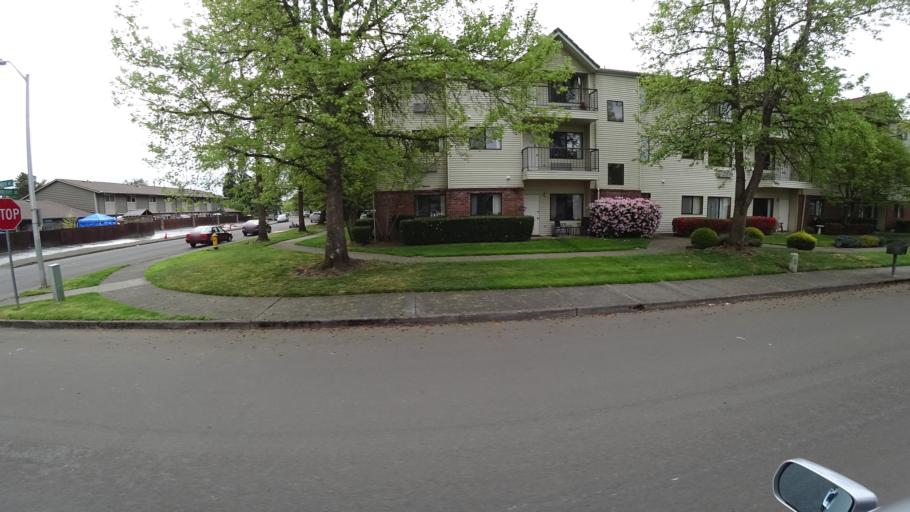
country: US
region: Oregon
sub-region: Washington County
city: Hillsboro
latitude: 45.5323
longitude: -122.9660
